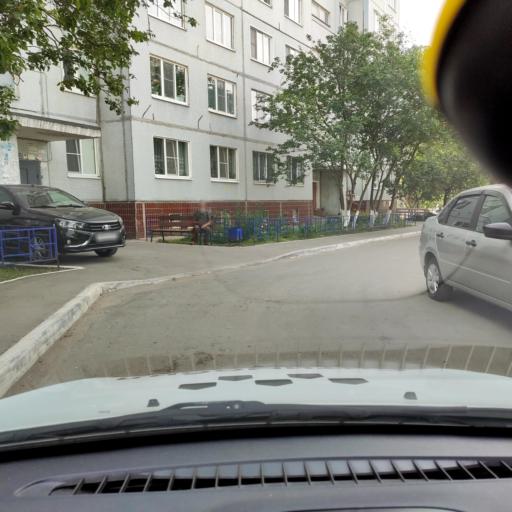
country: RU
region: Samara
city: Zhigulevsk
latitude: 53.4030
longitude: 49.5310
